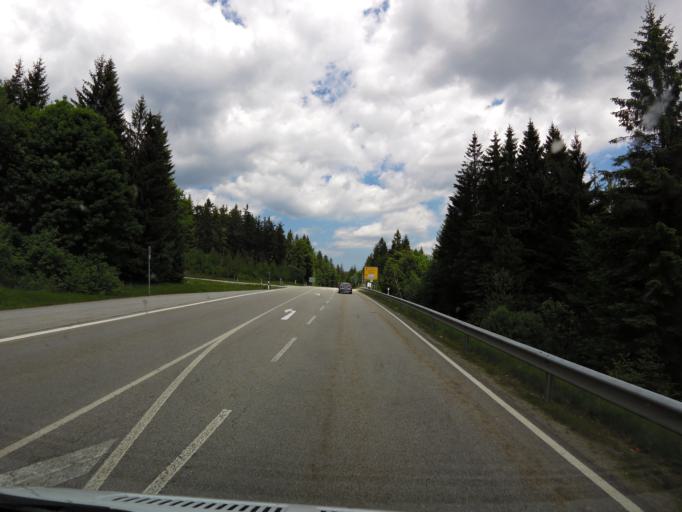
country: DE
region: Bavaria
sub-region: Lower Bavaria
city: Philippsreut
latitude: 48.8697
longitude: 13.6849
